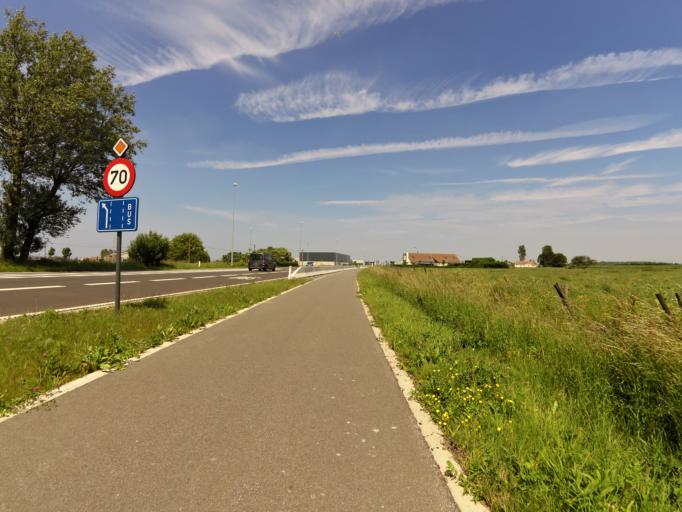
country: BE
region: Flanders
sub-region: Provincie West-Vlaanderen
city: Ostend
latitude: 51.1852
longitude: 2.8990
